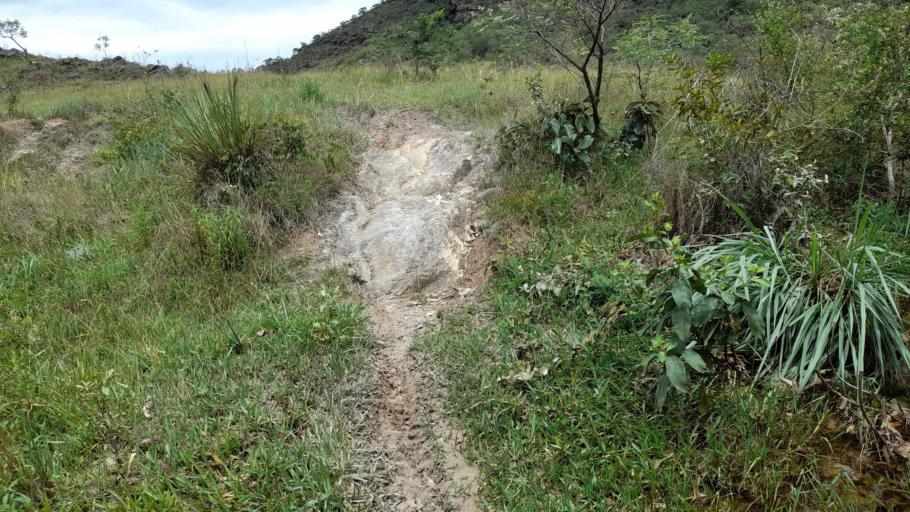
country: BR
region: Minas Gerais
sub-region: Sao Joao Del Rei
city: Sao Joao del Rei
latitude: -21.1240
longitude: -44.2761
